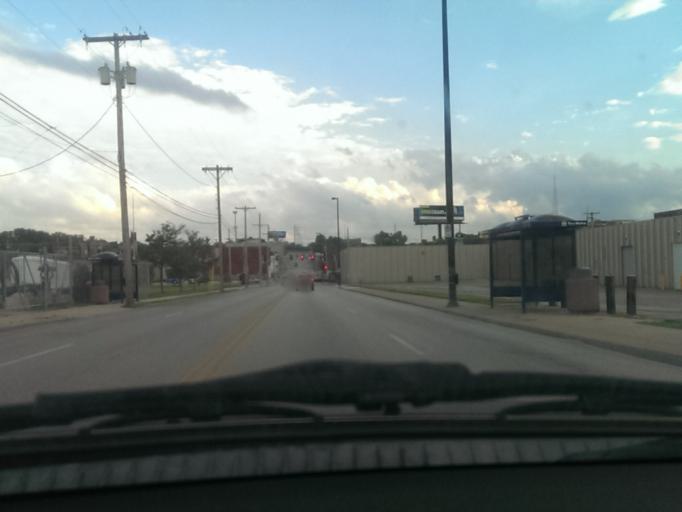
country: US
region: Missouri
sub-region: Jackson County
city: Kansas City
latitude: 39.0929
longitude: -94.5702
